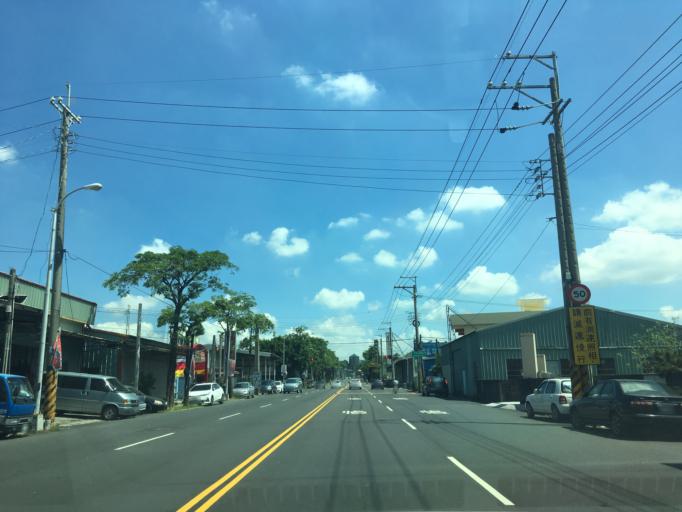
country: TW
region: Taiwan
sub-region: Taichung City
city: Taichung
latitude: 24.1869
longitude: 120.7186
